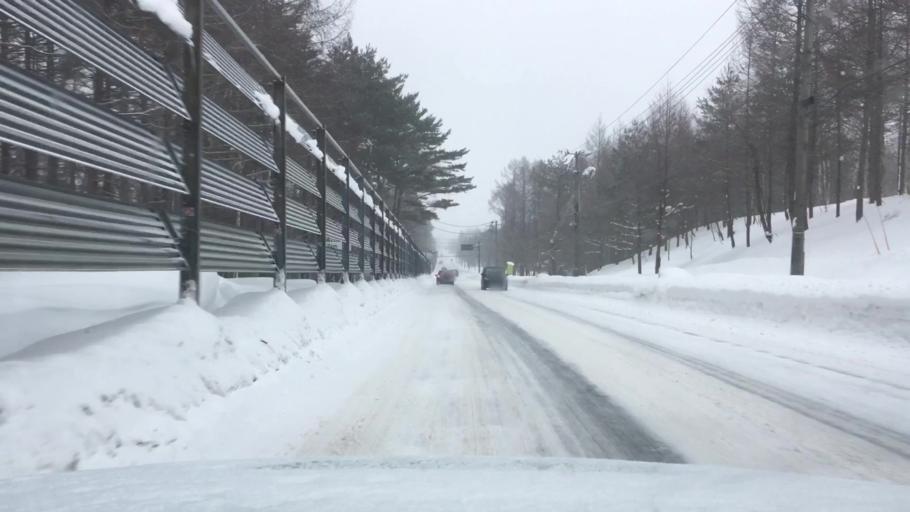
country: JP
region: Akita
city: Hanawa
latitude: 40.0052
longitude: 140.9717
